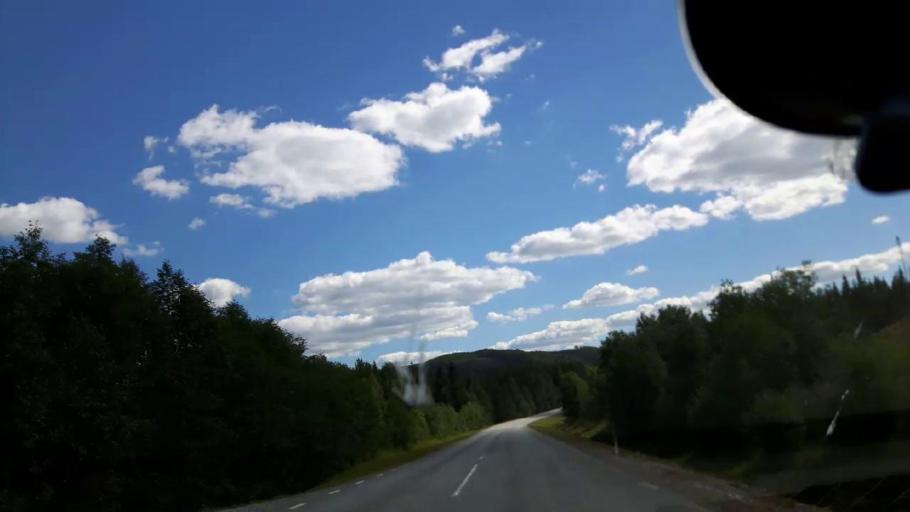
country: SE
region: Jaemtland
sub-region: Ragunda Kommun
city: Hammarstrand
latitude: 62.9564
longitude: 16.2063
